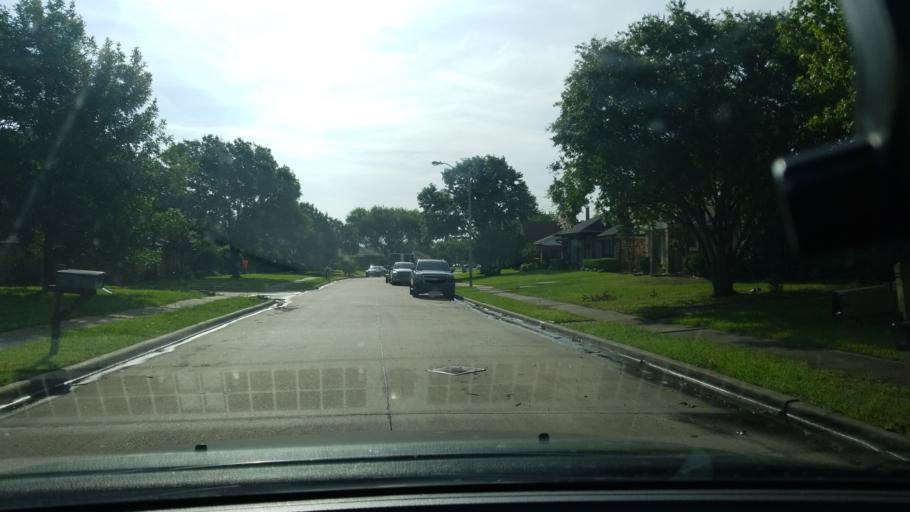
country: US
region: Texas
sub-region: Dallas County
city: Mesquite
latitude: 32.8004
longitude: -96.6138
